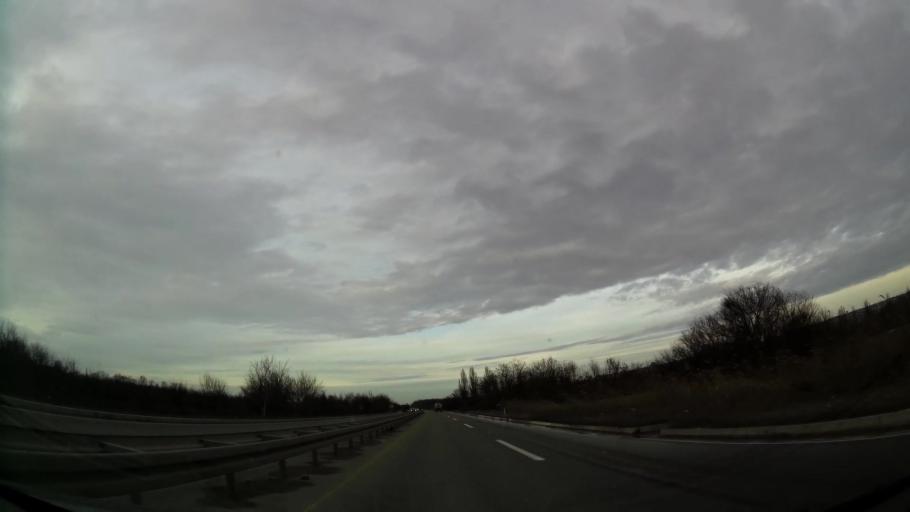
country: RS
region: Central Serbia
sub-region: Belgrade
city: Cukarica
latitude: 44.7580
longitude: 20.3852
